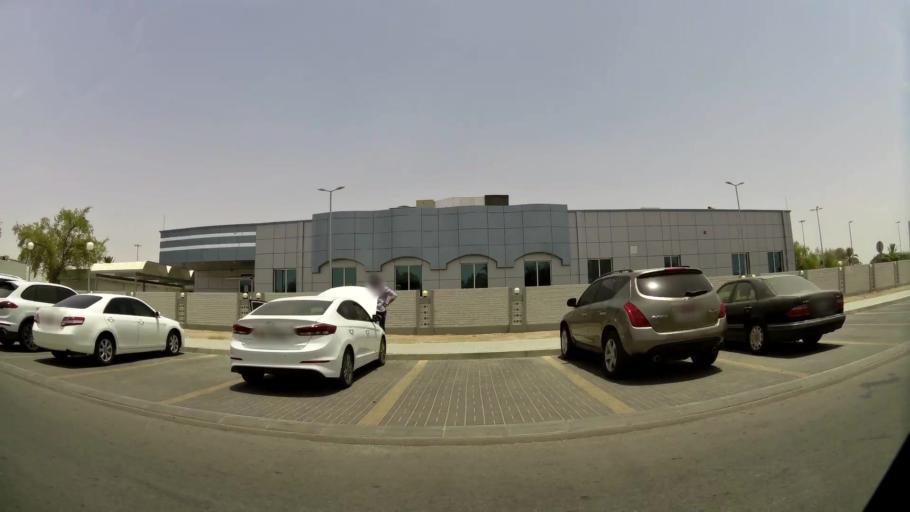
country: AE
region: Abu Dhabi
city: Al Ain
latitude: 24.2123
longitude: 55.7488
